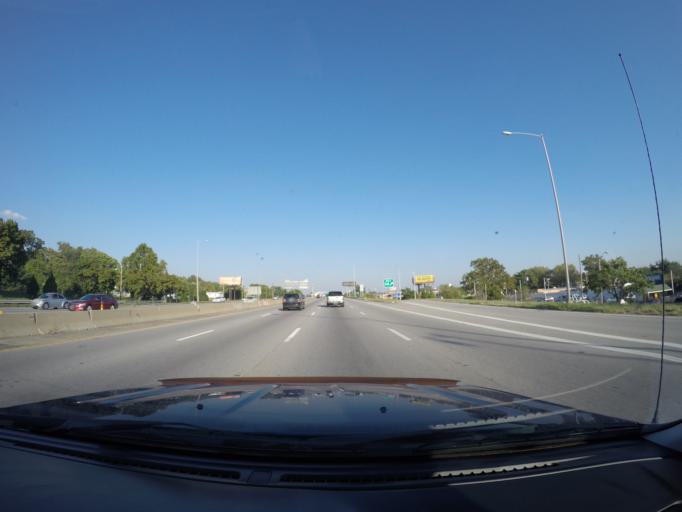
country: US
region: Missouri
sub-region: Jackson County
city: Kansas City
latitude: 39.0958
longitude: -94.5587
